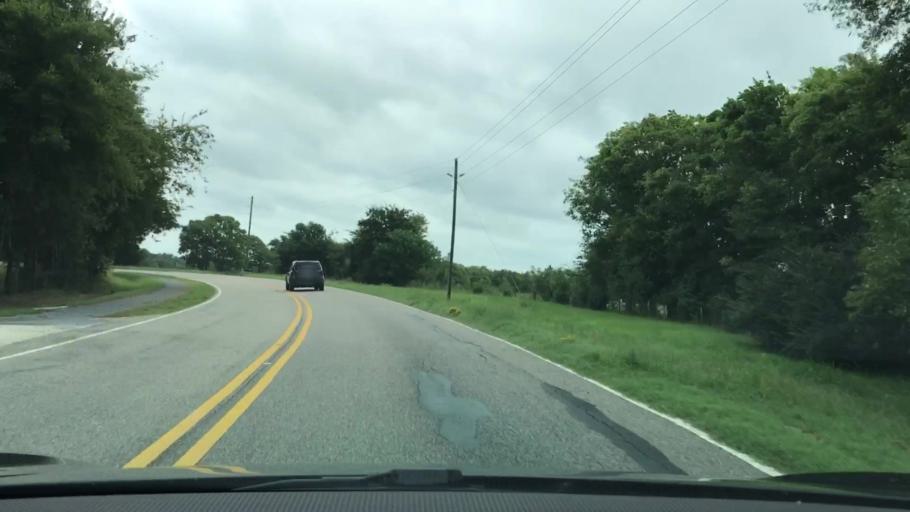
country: US
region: Alabama
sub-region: Montgomery County
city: Pike Road
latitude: 32.3028
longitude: -86.0513
